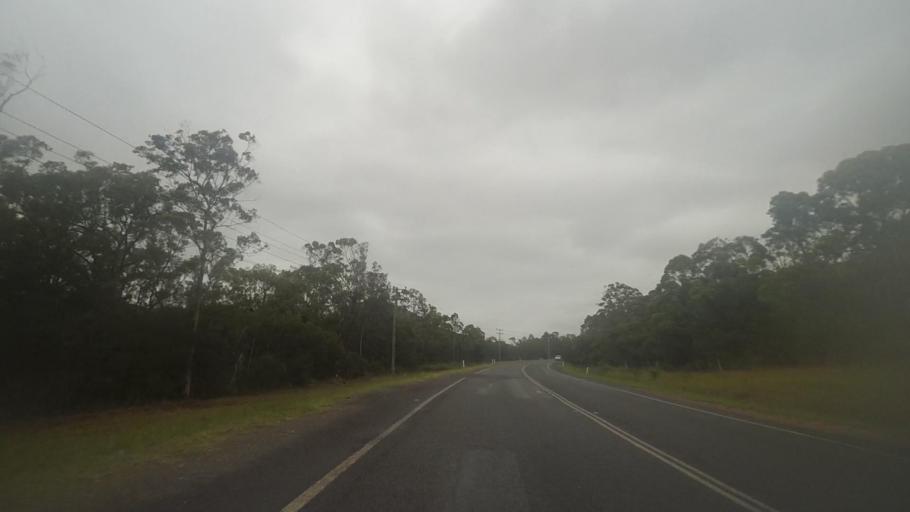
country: AU
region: New South Wales
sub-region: Port Stephens Shire
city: Port Stephens
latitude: -32.6370
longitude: 151.9947
